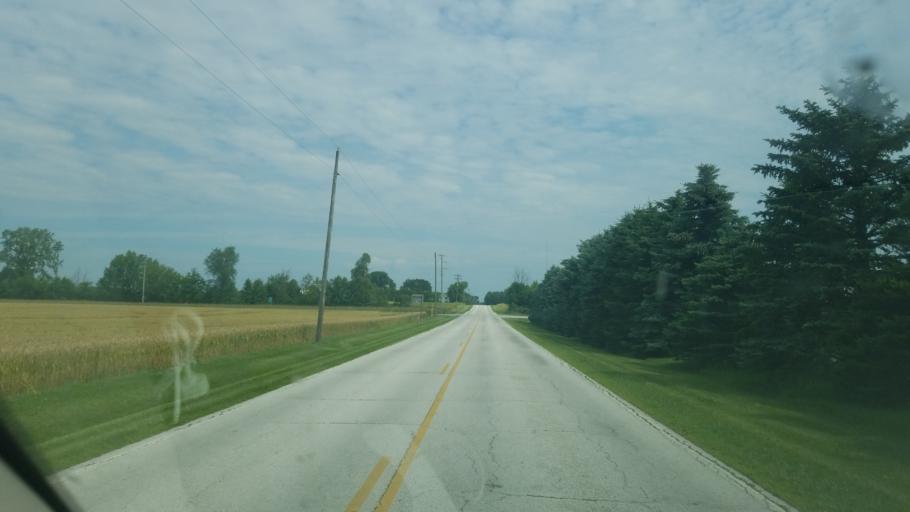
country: US
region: Ohio
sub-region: Seneca County
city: Fostoria
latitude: 41.0924
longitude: -83.4784
